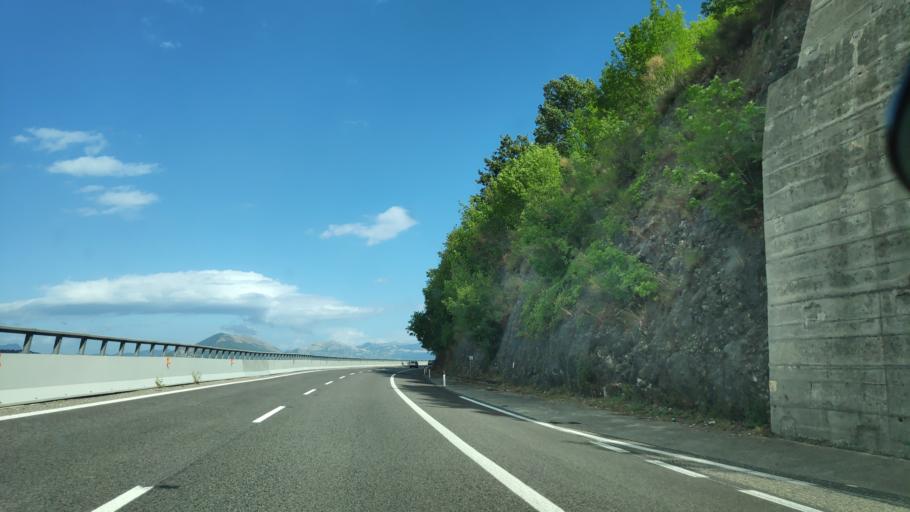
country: IT
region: Campania
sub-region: Provincia di Salerno
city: Sicignano degli Alburni
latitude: 40.5985
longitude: 15.3149
